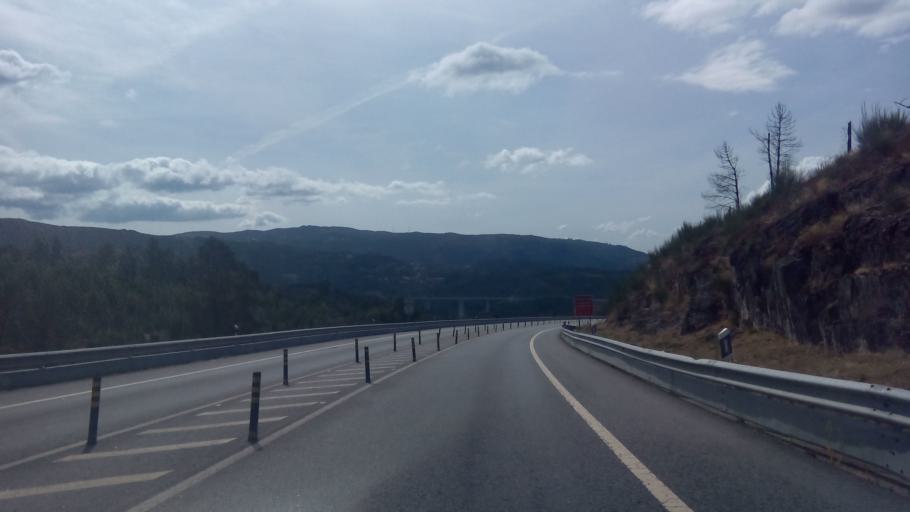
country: PT
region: Porto
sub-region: Amarante
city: Amarante
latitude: 41.2642
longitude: -7.9729
